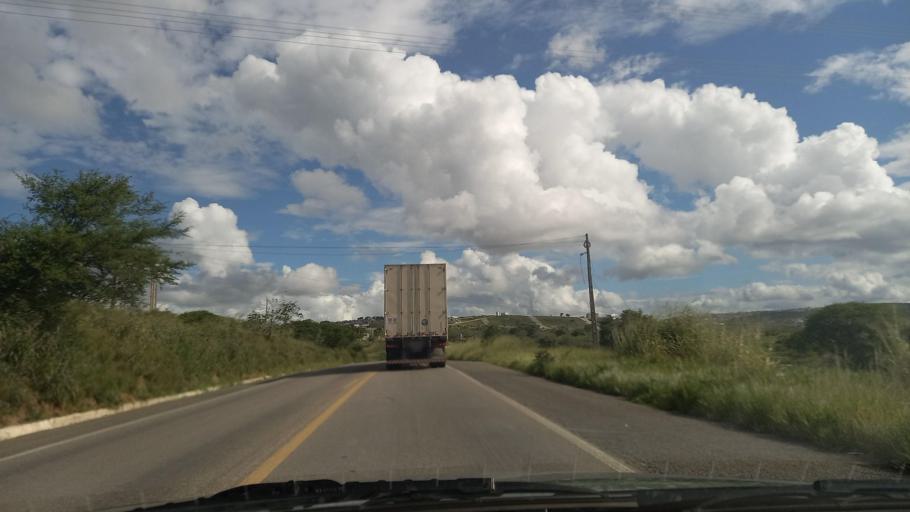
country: BR
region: Pernambuco
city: Garanhuns
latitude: -8.8492
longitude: -36.4613
